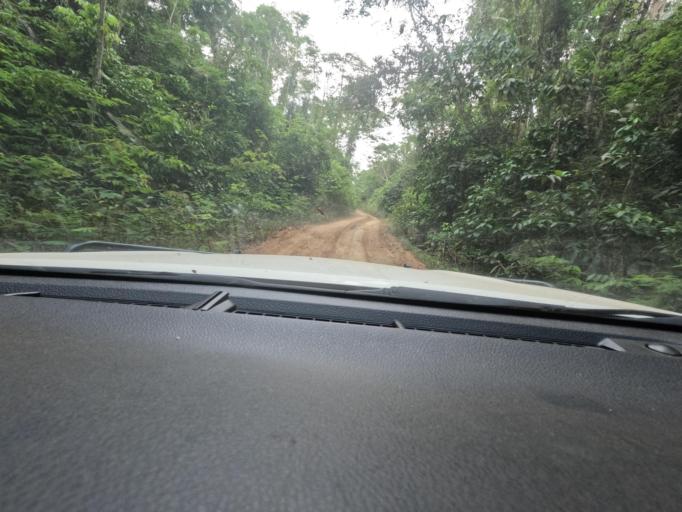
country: BR
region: Rondonia
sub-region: Porto Velho
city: Porto Velho
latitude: -8.6548
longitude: -63.1559
